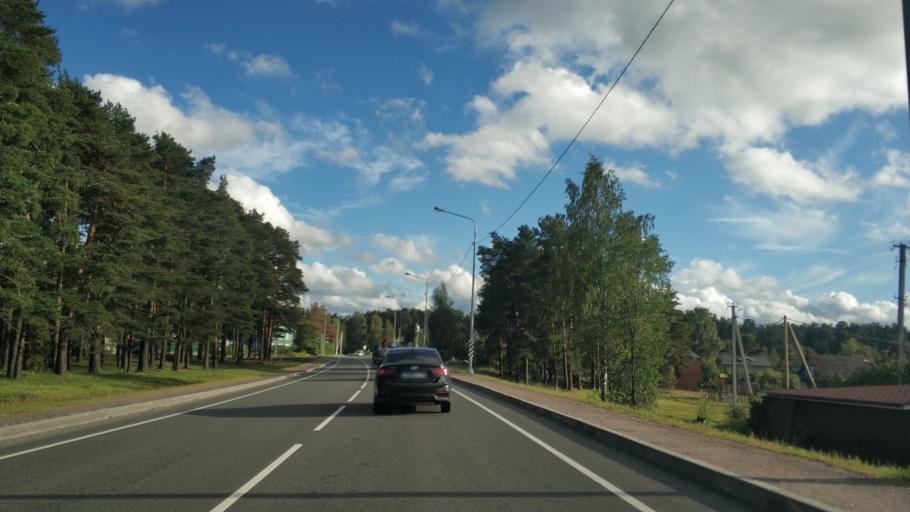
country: RU
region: Leningrad
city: Priozersk
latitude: 61.0009
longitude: 30.1817
